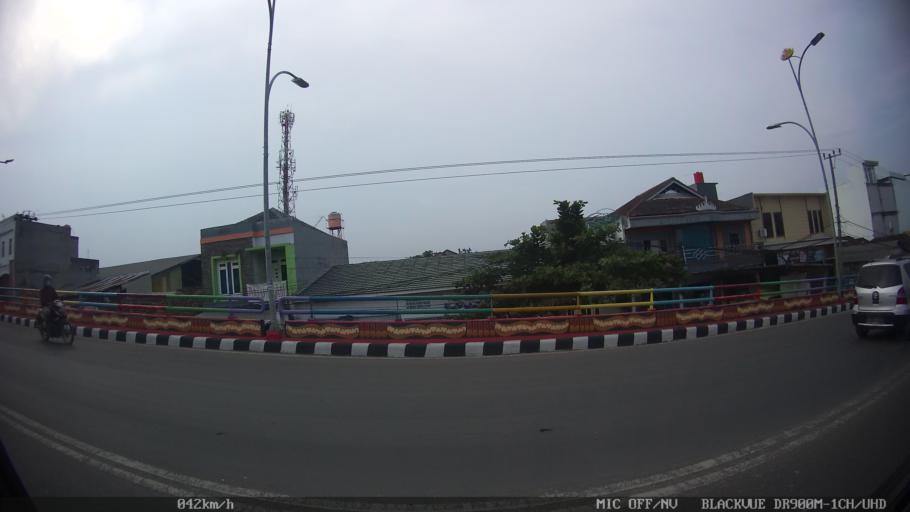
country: ID
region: Lampung
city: Kedaton
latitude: -5.3988
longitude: 105.2886
